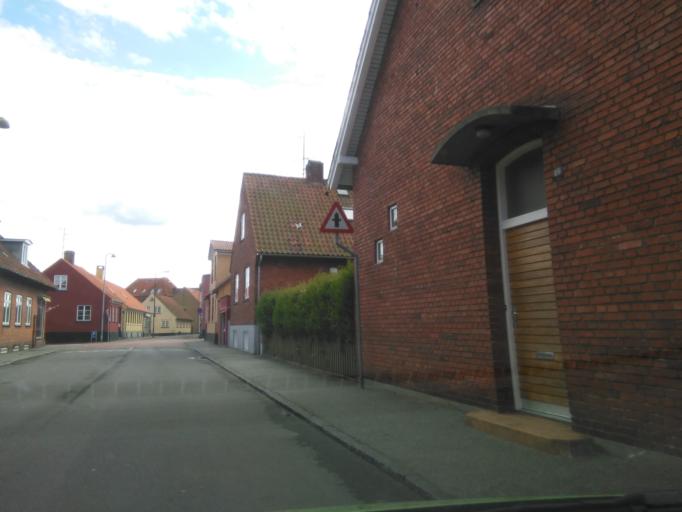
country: DK
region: Capital Region
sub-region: Bornholm Kommune
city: Nexo
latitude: 55.0646
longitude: 15.1325
